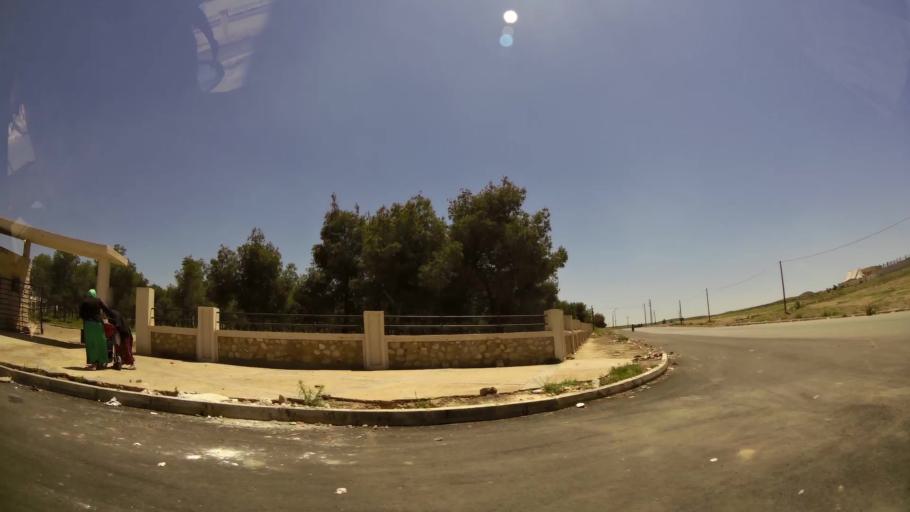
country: MA
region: Oriental
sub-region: Oujda-Angad
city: Oujda
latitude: 34.6542
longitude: -1.9241
